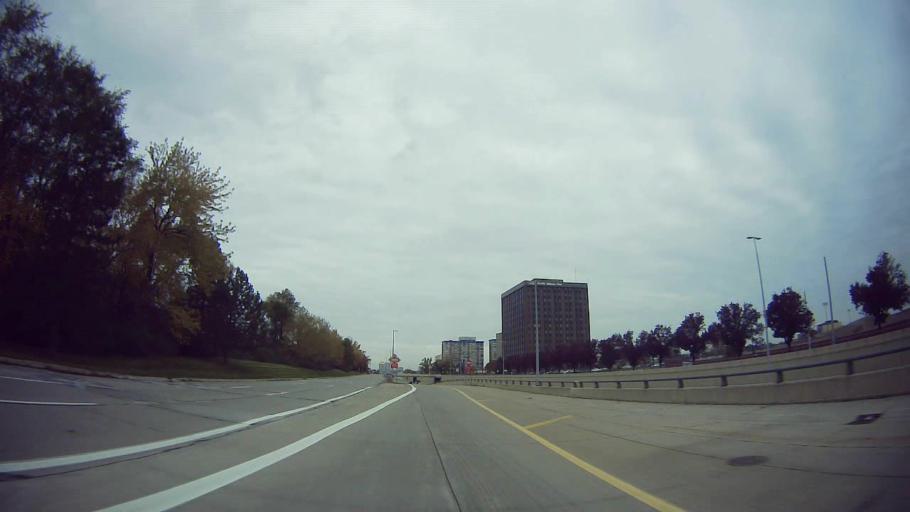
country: US
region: Michigan
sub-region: Oakland County
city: Southfield
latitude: 42.4495
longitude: -83.2087
